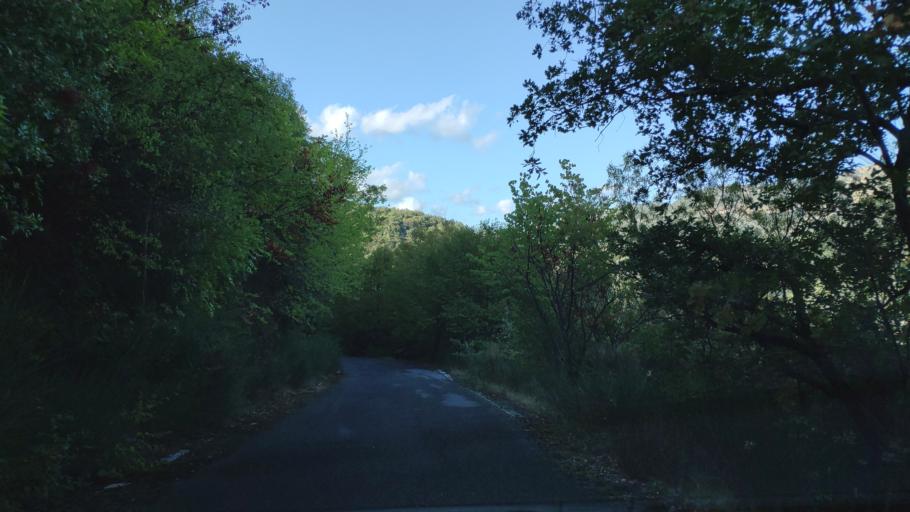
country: GR
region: Peloponnese
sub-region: Nomos Arkadias
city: Dimitsana
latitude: 37.5568
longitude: 22.0446
